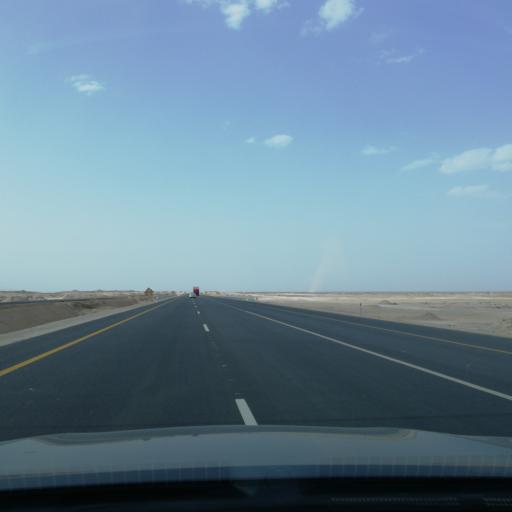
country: OM
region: Muhafazat ad Dakhiliyah
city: Adam
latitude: 22.0690
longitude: 57.5142
